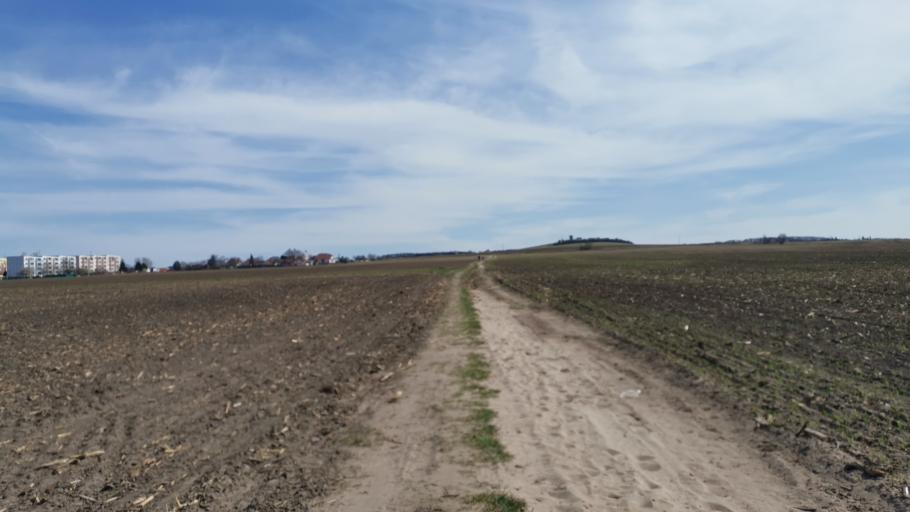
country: SK
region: Trnavsky
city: Gbely
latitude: 48.7136
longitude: 17.1124
